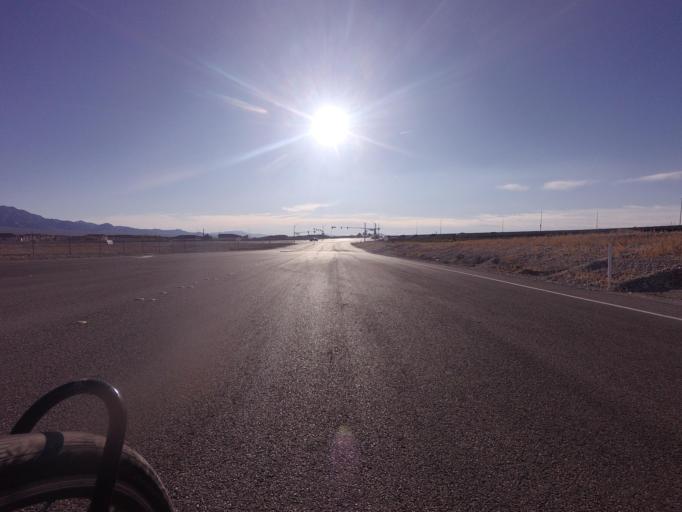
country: US
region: Nevada
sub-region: Clark County
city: Summerlin South
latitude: 36.3162
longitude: -115.2997
